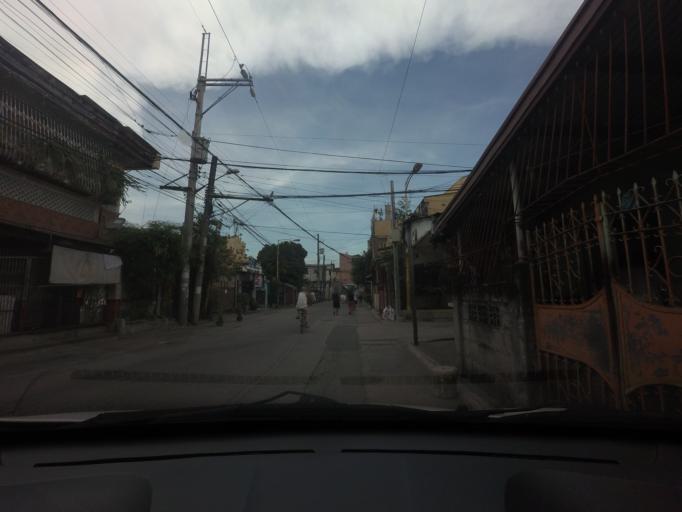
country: PH
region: Calabarzon
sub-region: Province of Rizal
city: Pateros
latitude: 14.5388
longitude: 121.0620
